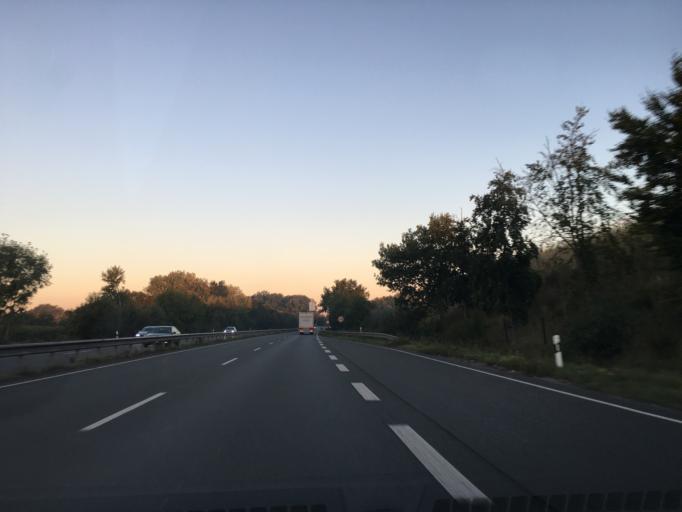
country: DE
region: North Rhine-Westphalia
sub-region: Regierungsbezirk Munster
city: Altenberge
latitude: 51.9930
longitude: 7.5377
